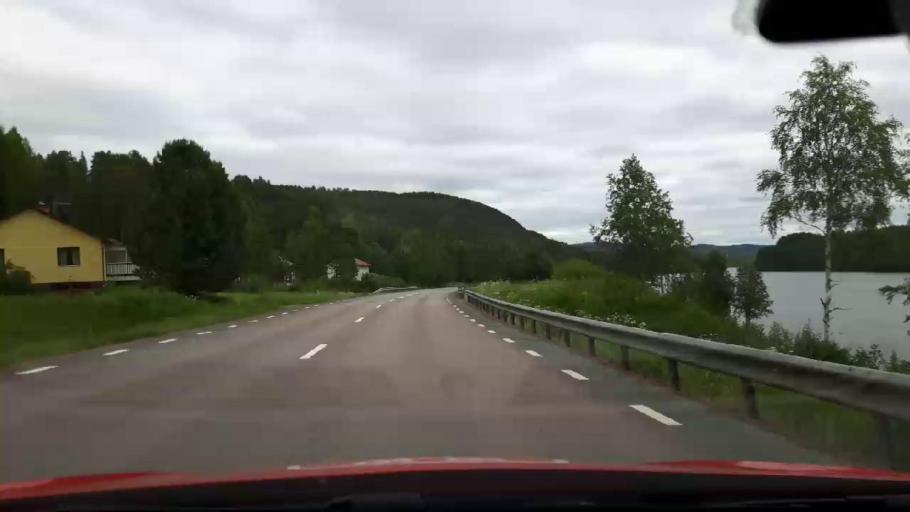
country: SE
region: Jaemtland
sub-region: Ragunda Kommun
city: Hammarstrand
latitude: 63.1449
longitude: 16.3304
